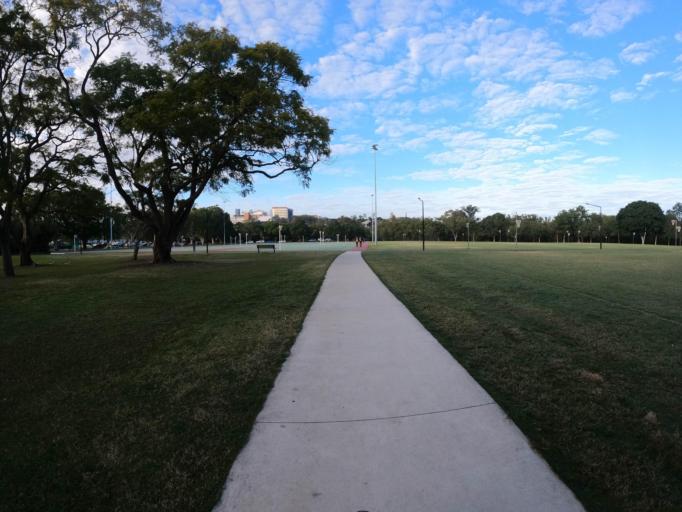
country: AU
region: Queensland
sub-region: Brisbane
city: Windsor
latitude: -27.4421
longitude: 153.0251
